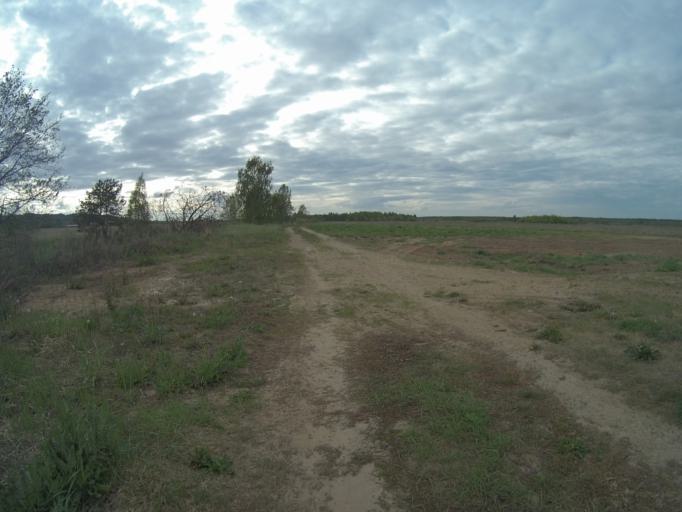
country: RU
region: Vladimir
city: Raduzhnyy
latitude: 56.0150
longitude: 40.3710
